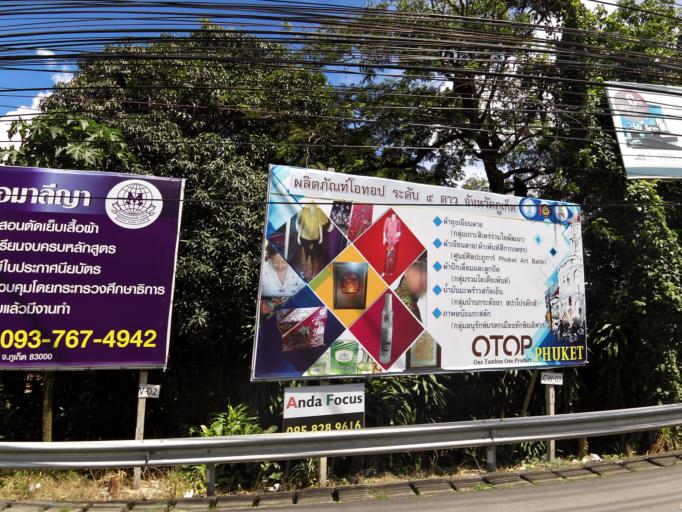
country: TH
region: Phuket
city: Mueang Phuket
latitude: 7.8732
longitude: 98.3634
